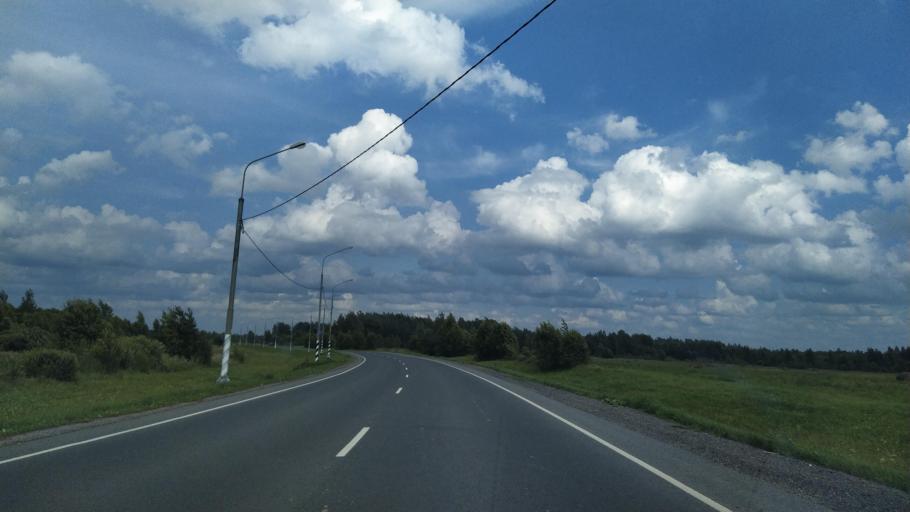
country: RU
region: Pskov
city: Dno
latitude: 58.0627
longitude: 30.0267
